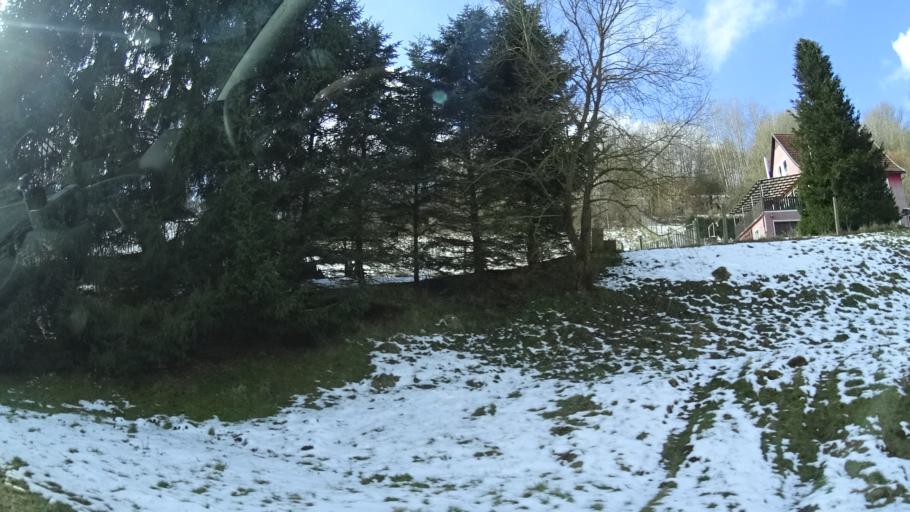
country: DE
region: Thuringia
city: Schwarza
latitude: 50.6141
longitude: 10.5248
